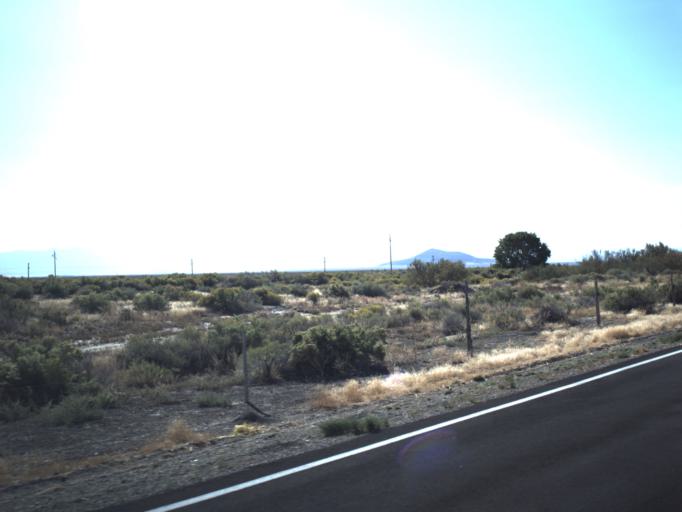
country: US
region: Utah
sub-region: Millard County
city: Delta
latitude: 39.2602
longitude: -112.6532
